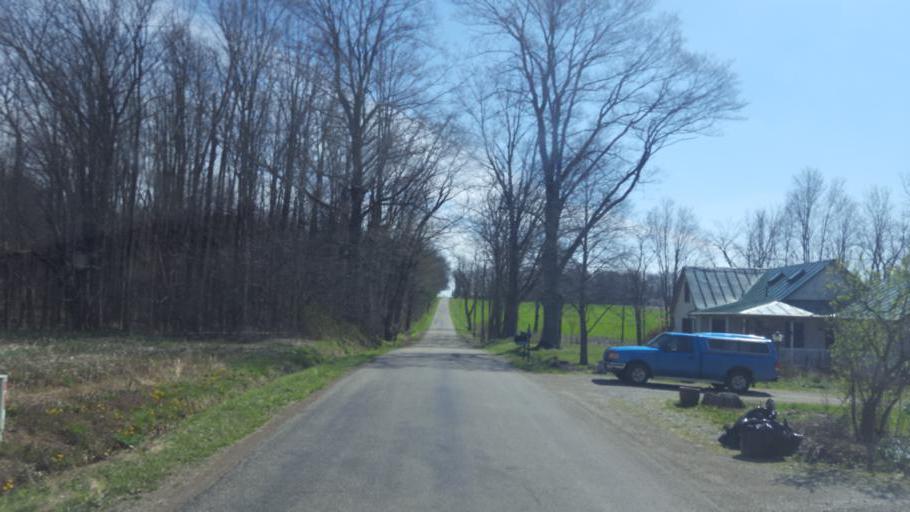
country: US
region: Ohio
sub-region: Knox County
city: Gambier
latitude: 40.3617
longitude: -82.4381
